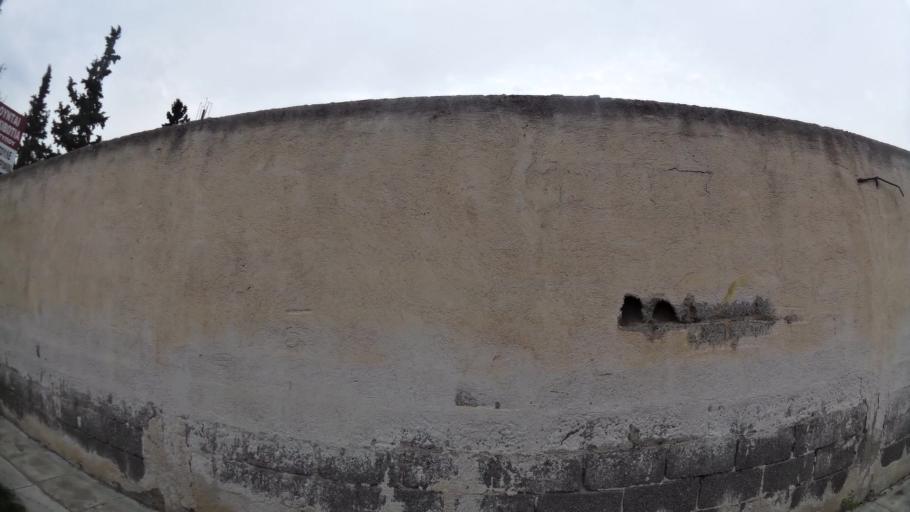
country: GR
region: Attica
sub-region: Nomarchia Athinas
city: Tavros
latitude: 37.9720
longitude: 23.6787
